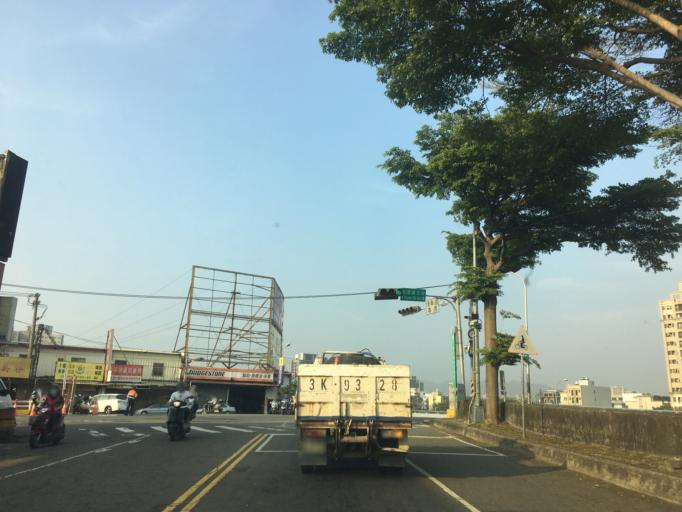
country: TW
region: Taiwan
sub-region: Taichung City
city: Taichung
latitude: 24.1644
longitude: 120.7041
